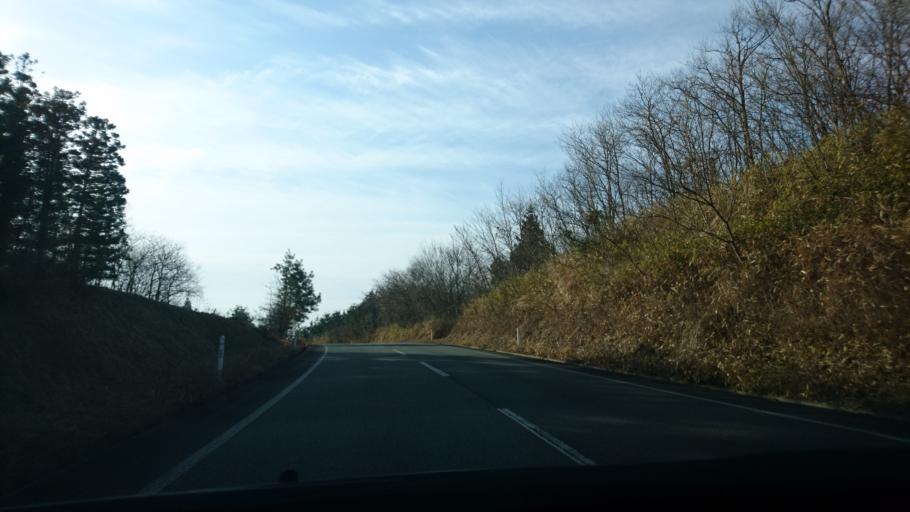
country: JP
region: Iwate
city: Ichinoseki
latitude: 38.8564
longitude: 141.2009
